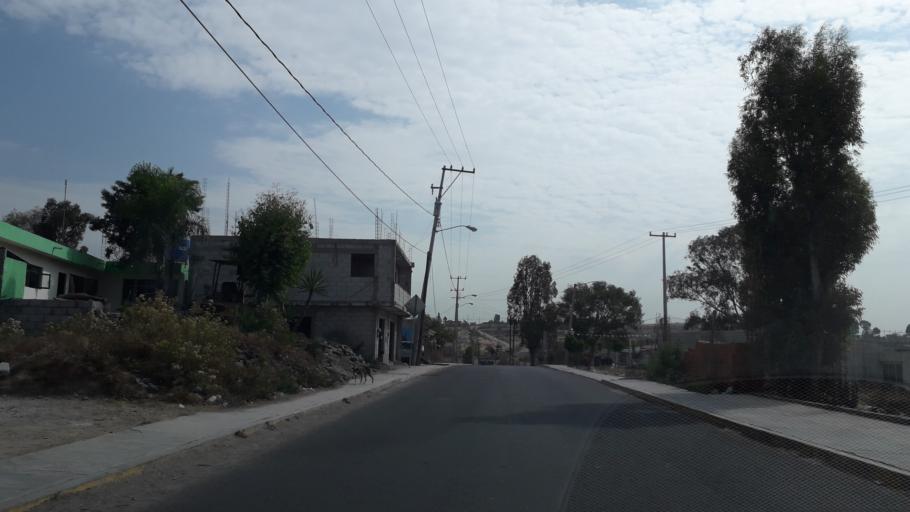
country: MX
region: Puebla
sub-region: Puebla
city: San Andres Azumiatla
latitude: 18.9082
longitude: -98.2433
